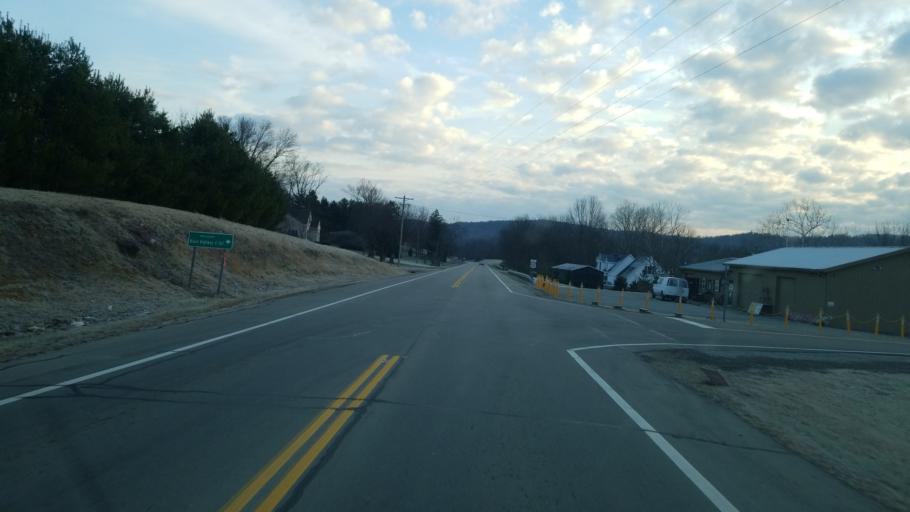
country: US
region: Ohio
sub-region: Ross County
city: North Fork Village
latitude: 39.3112
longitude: -83.1206
